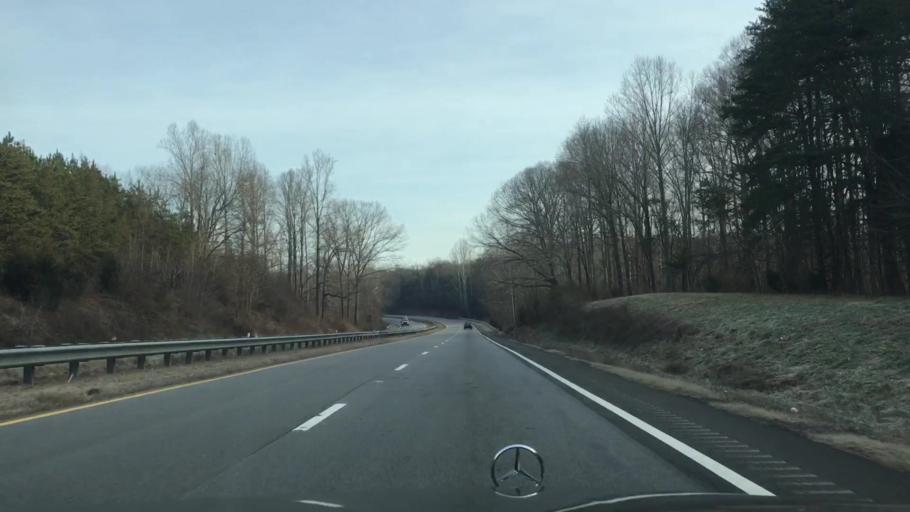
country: US
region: Virginia
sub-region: Pittsylvania County
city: Chatham
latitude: 36.8137
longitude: -79.3853
